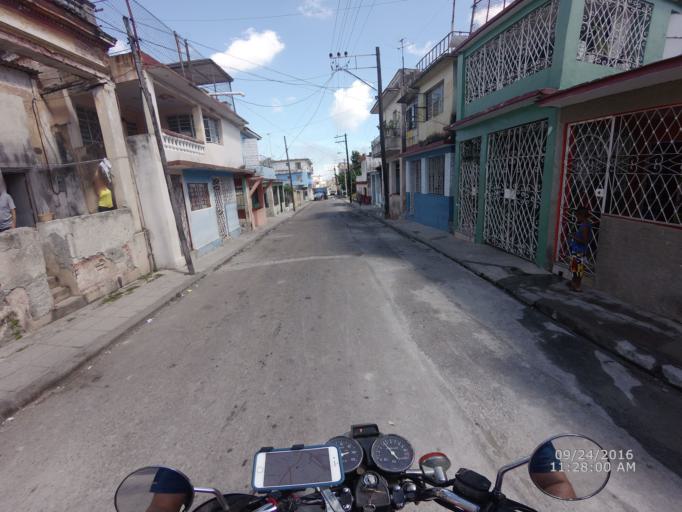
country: CU
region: La Habana
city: Cerro
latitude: 23.1104
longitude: -82.3648
